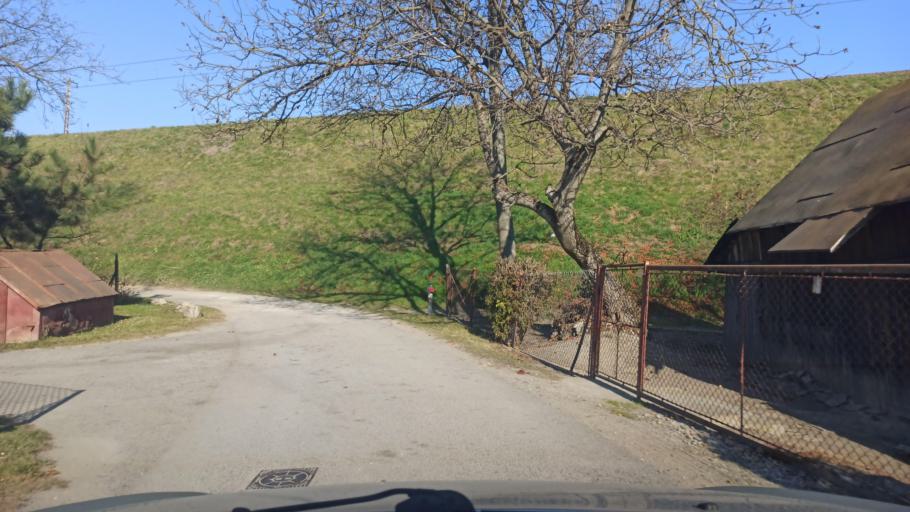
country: PL
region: Subcarpathian Voivodeship
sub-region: Powiat jaroslawski
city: Radymno
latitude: 49.9428
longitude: 22.8176
